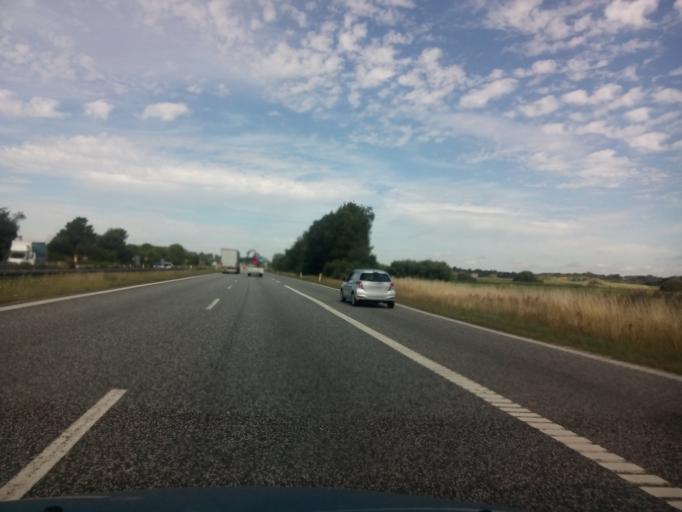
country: DK
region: Central Jutland
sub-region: Randers Kommune
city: Randers
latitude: 56.4498
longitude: 10.0001
